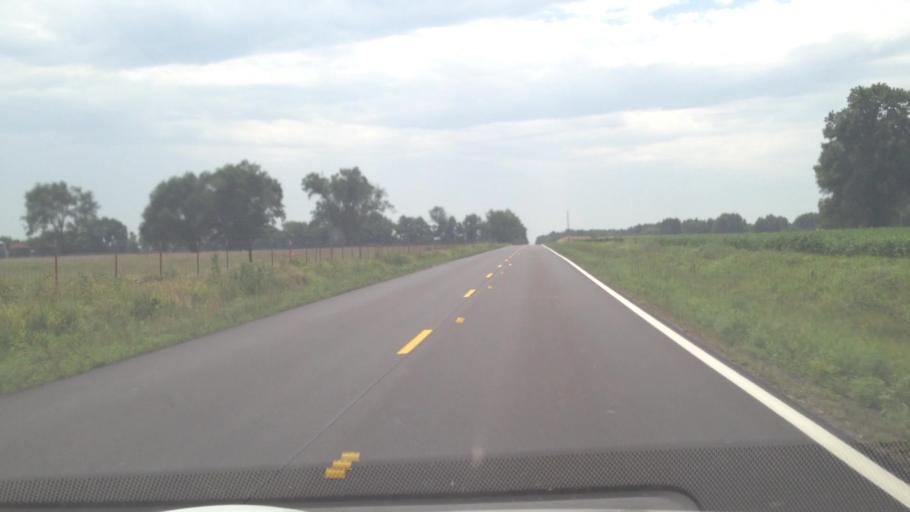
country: US
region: Kansas
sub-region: Crawford County
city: Girard
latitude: 37.5314
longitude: -94.9606
